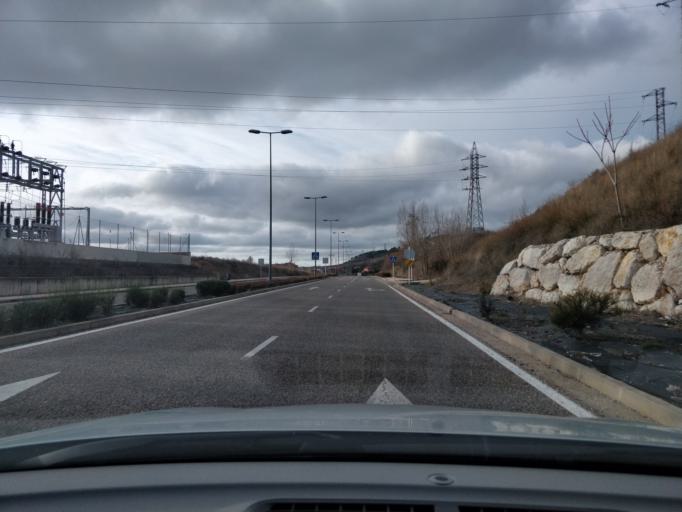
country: ES
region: Castille and Leon
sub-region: Provincia de Burgos
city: Villagonzalo-Pedernales
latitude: 42.3479
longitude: -3.7255
